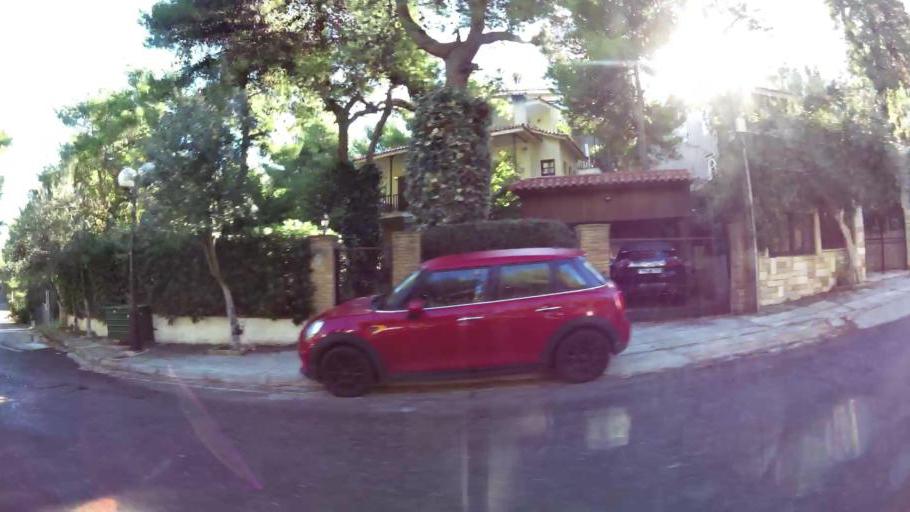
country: GR
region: Attica
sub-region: Nomarchia Anatolikis Attikis
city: Stamata
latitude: 38.1329
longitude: 23.8735
